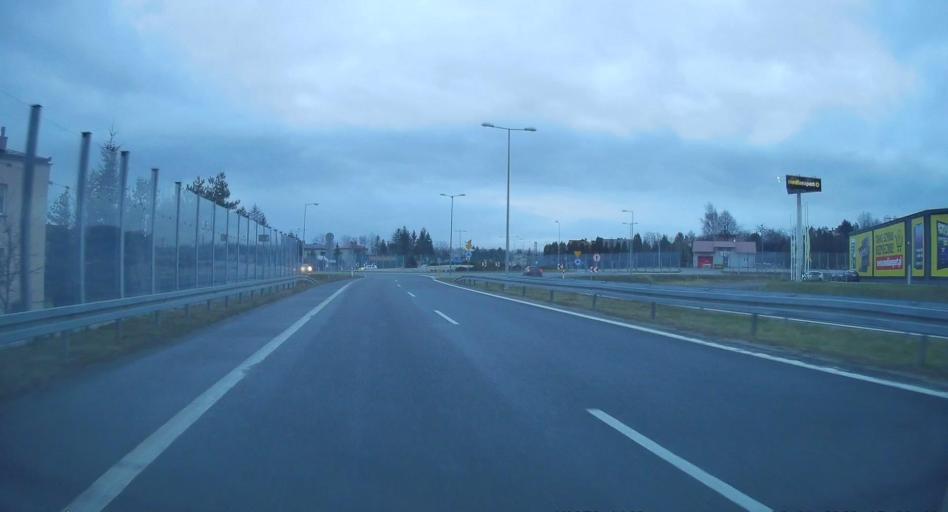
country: PL
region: Subcarpathian Voivodeship
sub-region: Powiat ropczycko-sedziszowski
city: Ropczyce
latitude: 50.0565
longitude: 21.6305
